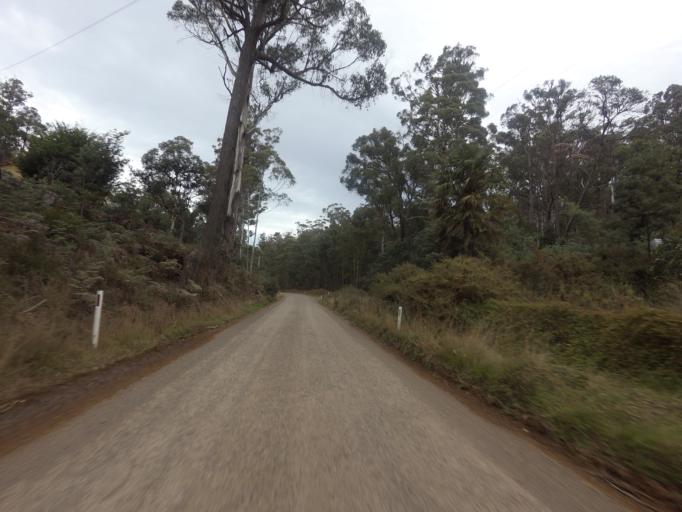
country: AU
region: Tasmania
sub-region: Derwent Valley
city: New Norfolk
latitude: -42.5828
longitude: 147.0083
